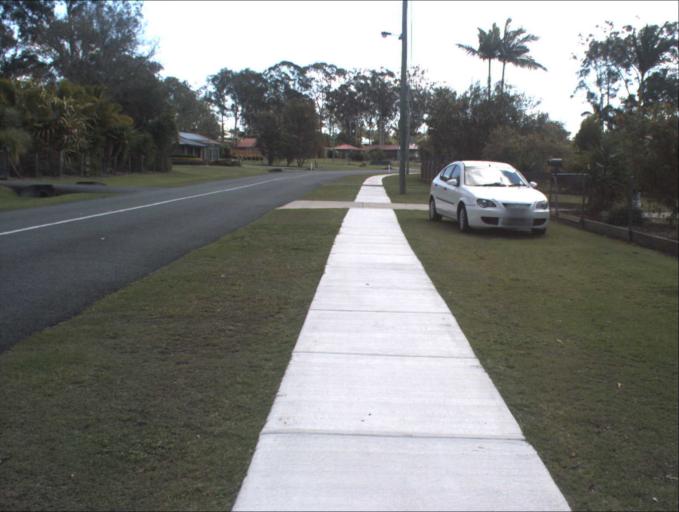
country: AU
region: Queensland
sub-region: Logan
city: Park Ridge South
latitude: -27.7311
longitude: 153.0461
